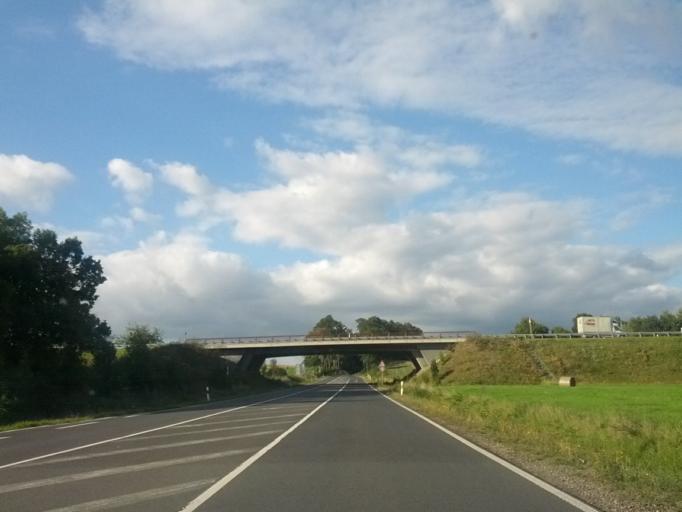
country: DE
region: Thuringia
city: Barchfeld
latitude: 50.8122
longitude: 10.2918
